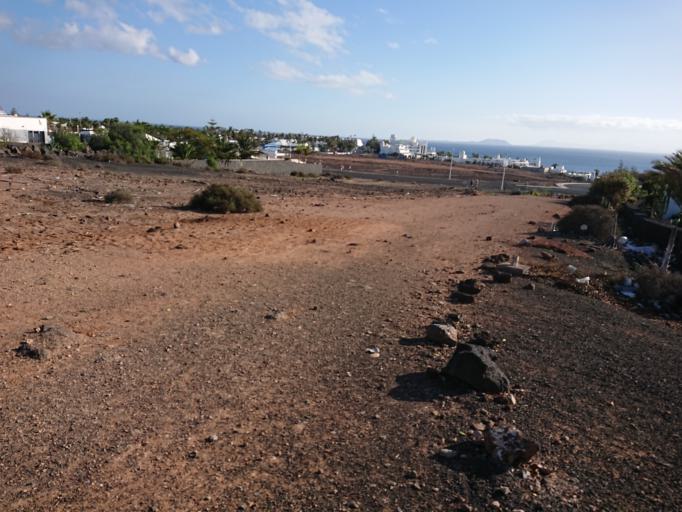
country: ES
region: Canary Islands
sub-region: Provincia de Las Palmas
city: Playa Blanca
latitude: 28.8649
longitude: -13.8460
